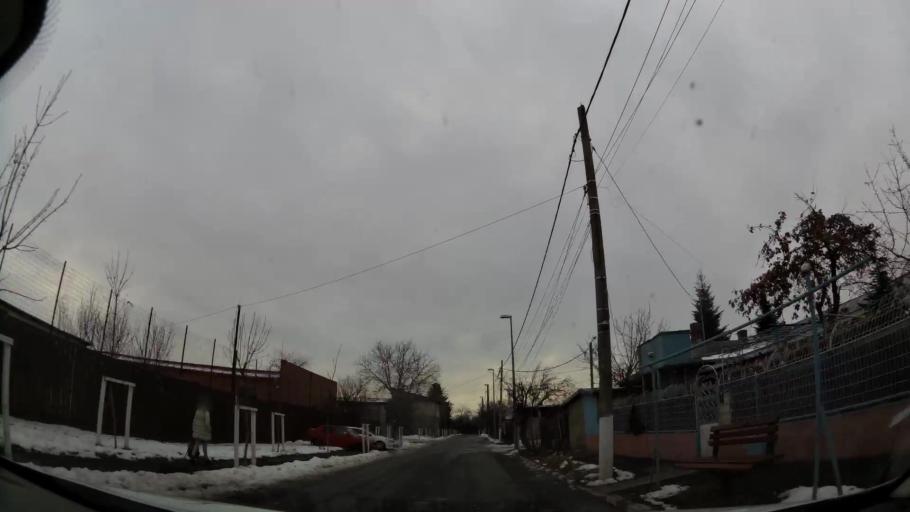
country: RO
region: Ilfov
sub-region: Voluntari City
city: Voluntari
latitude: 44.4853
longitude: 26.1702
